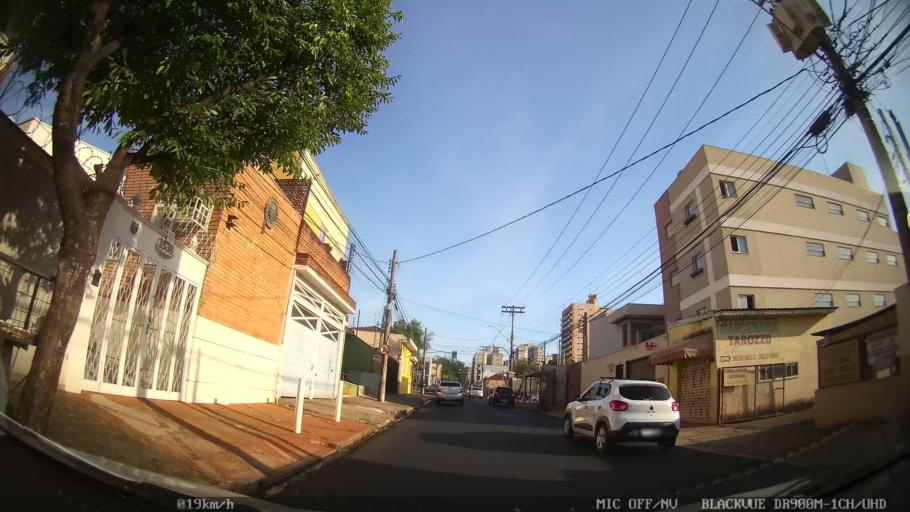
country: BR
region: Sao Paulo
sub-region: Ribeirao Preto
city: Ribeirao Preto
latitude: -21.1838
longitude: -47.8026
